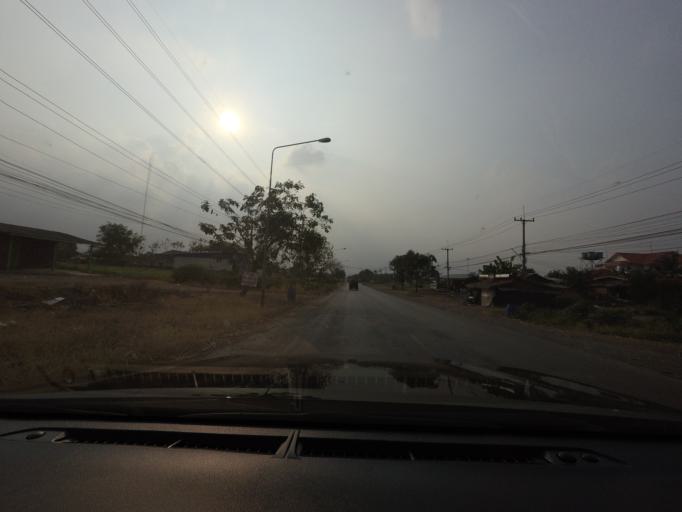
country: TH
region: Sara Buri
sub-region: Amphoe Wang Muang
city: Wang Muang
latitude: 14.8419
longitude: 101.0964
